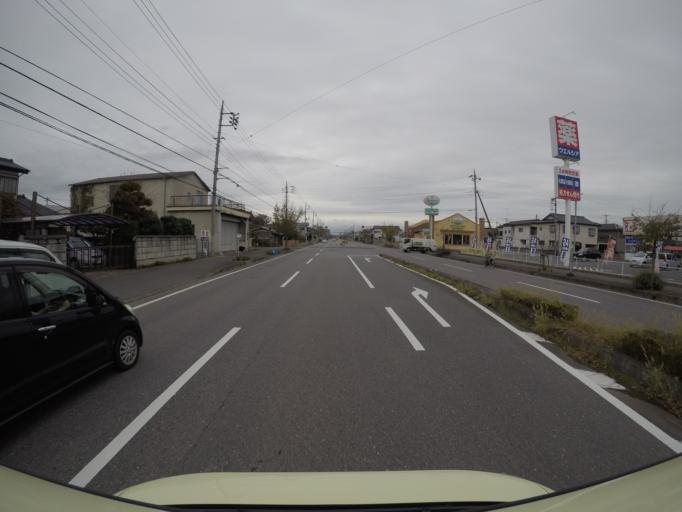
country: JP
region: Ibaraki
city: Naka
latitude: 36.0879
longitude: 140.1879
